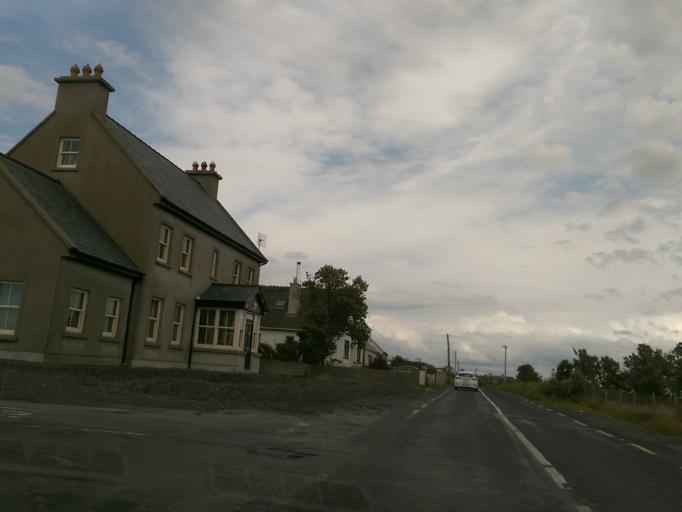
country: IE
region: Munster
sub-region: An Clar
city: Kilrush
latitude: 52.7222
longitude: -9.5808
